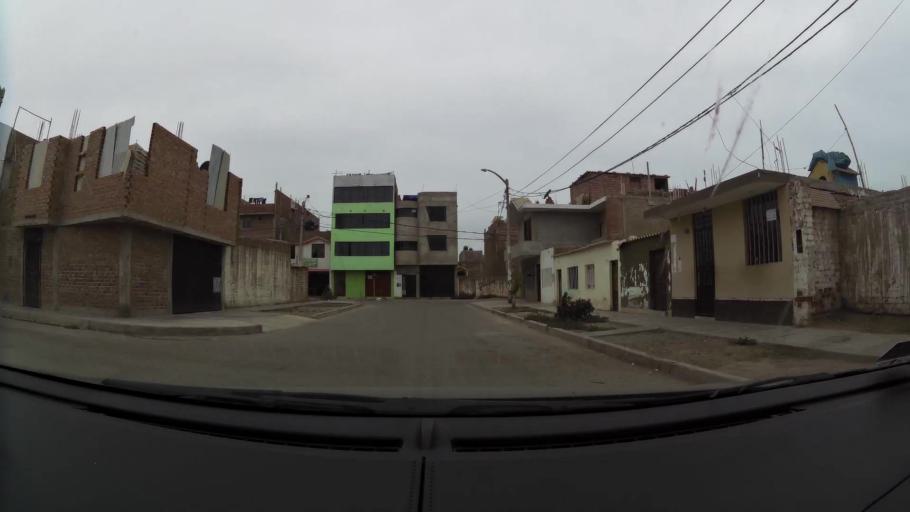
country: PE
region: La Libertad
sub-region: Provincia de Trujillo
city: Buenos Aires
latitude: -8.1428
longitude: -79.0468
